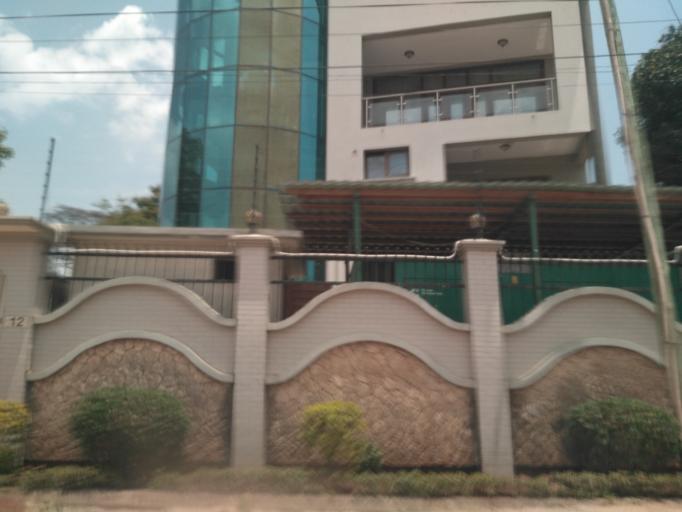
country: TZ
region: Dar es Salaam
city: Dar es Salaam
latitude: -6.8011
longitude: 39.2807
